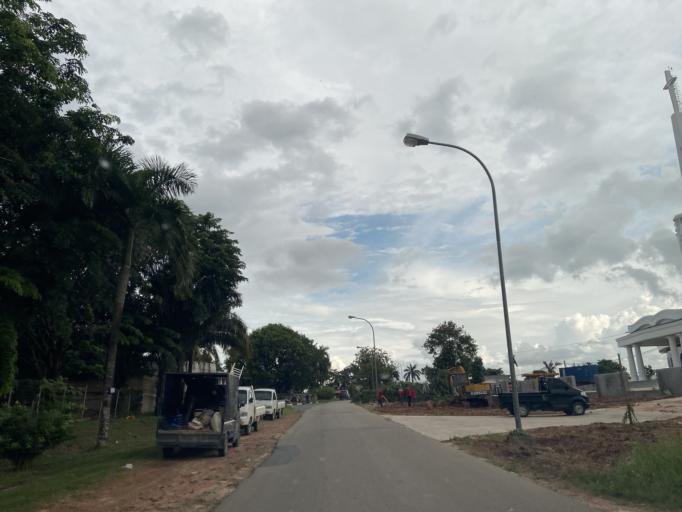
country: SG
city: Singapore
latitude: 1.1193
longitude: 104.0519
